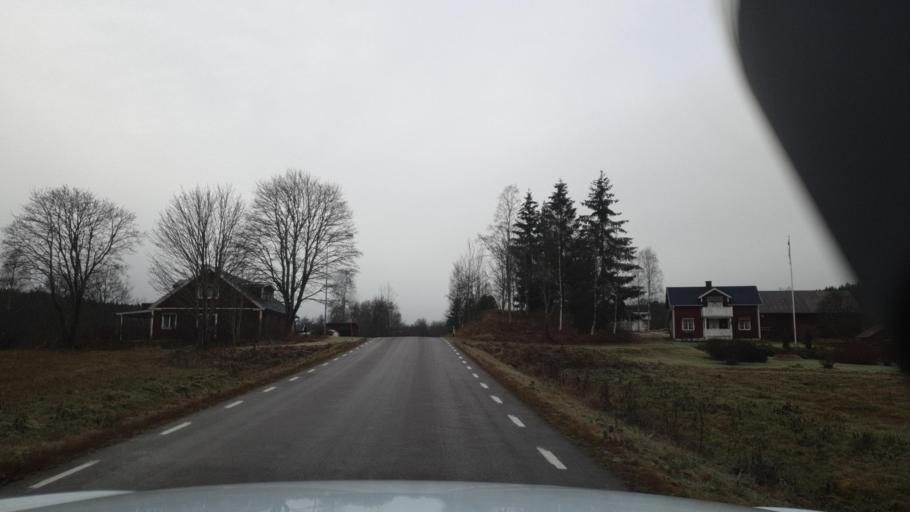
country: SE
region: Vaermland
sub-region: Arvika Kommun
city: Arvika
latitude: 59.7736
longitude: 12.7851
